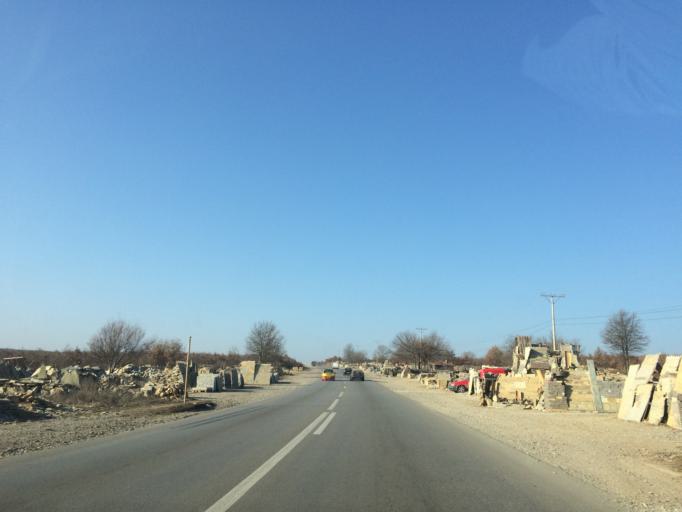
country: XK
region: Pec
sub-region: Komuna e Klines
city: Klina
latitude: 42.5955
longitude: 20.6507
